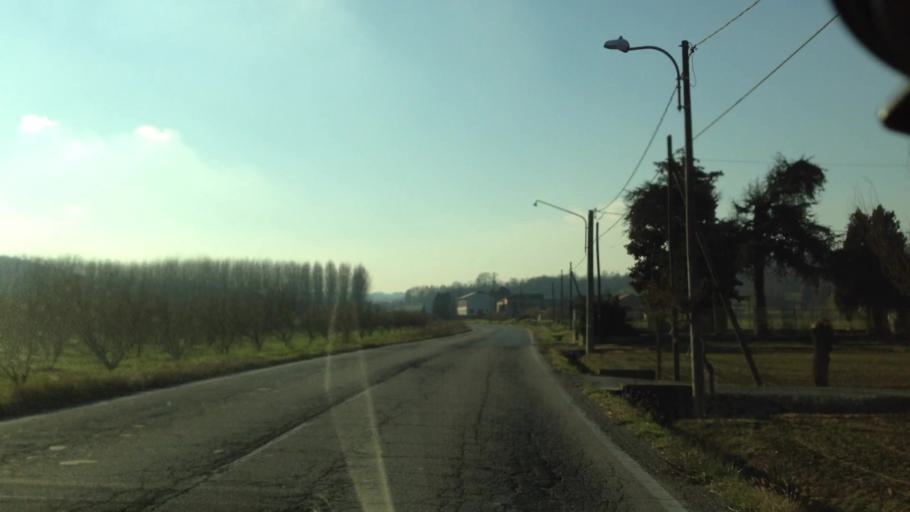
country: IT
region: Piedmont
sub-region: Provincia di Asti
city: Cortiglione
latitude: 44.8365
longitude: 8.3799
